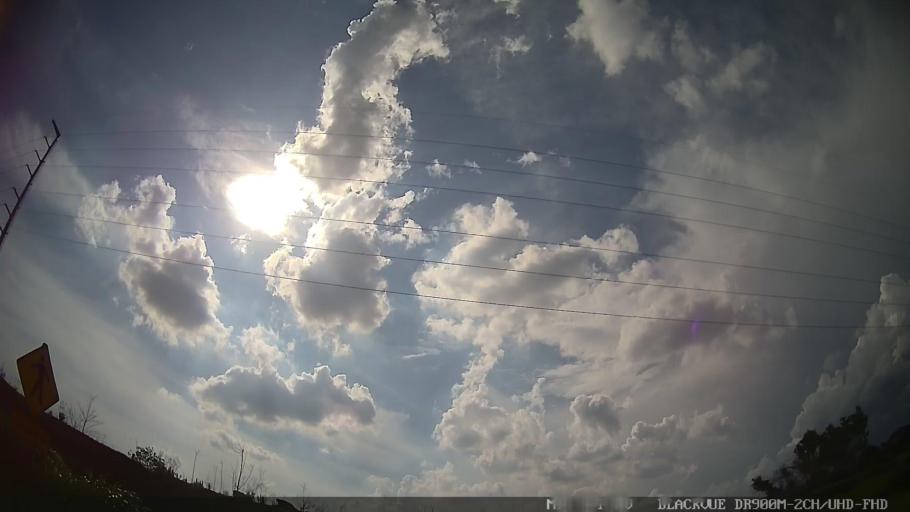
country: BR
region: Sao Paulo
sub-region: Braganca Paulista
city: Braganca Paulista
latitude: -22.9115
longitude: -46.5470
